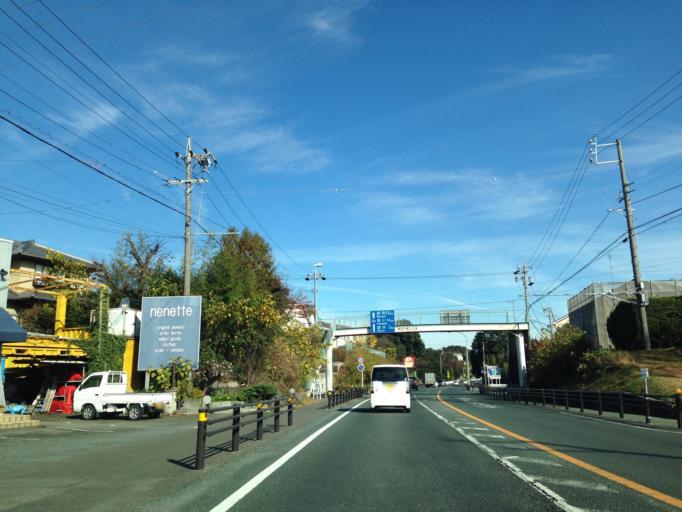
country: JP
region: Shizuoka
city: Iwata
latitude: 34.7301
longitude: 137.8703
